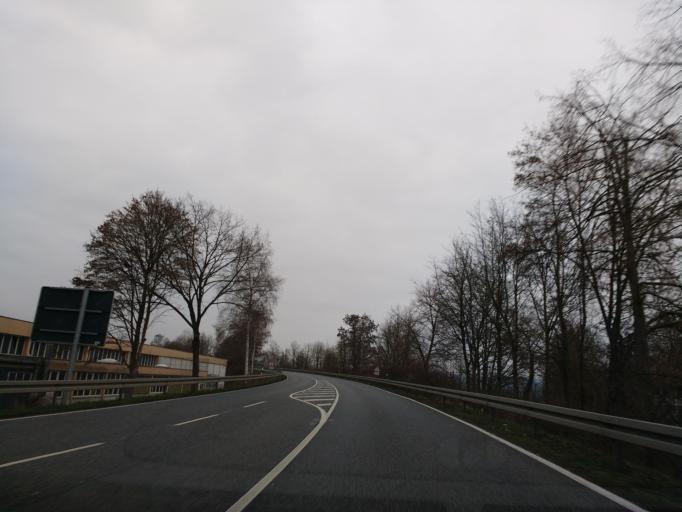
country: DE
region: Hesse
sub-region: Regierungsbezirk Kassel
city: Alheim
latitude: 51.0661
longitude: 9.6109
